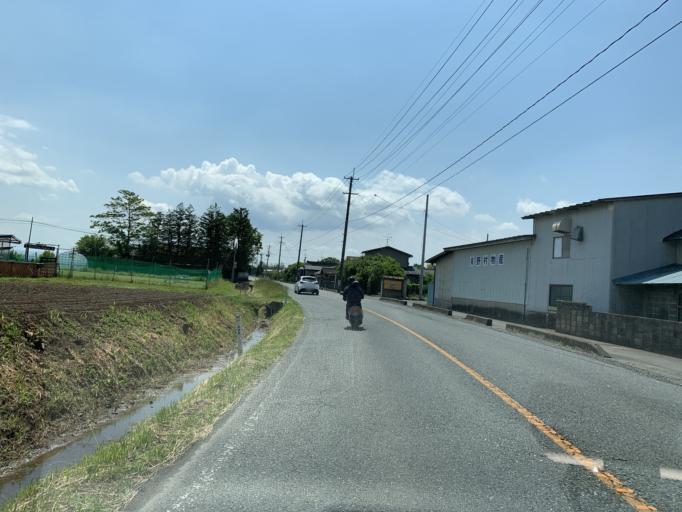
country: JP
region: Miyagi
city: Kogota
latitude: 38.5763
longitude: 141.0335
